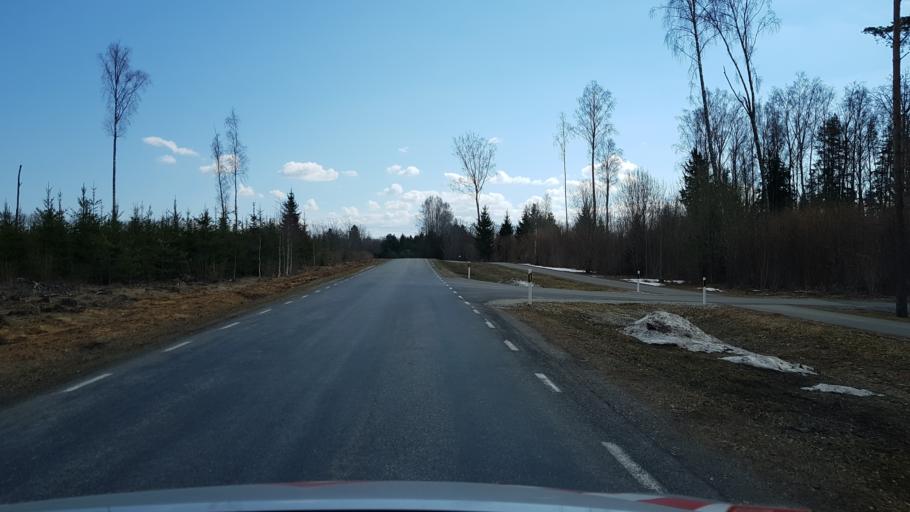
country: EE
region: Laeaene-Virumaa
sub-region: Rakvere linn
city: Rakvere
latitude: 59.3841
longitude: 26.3070
